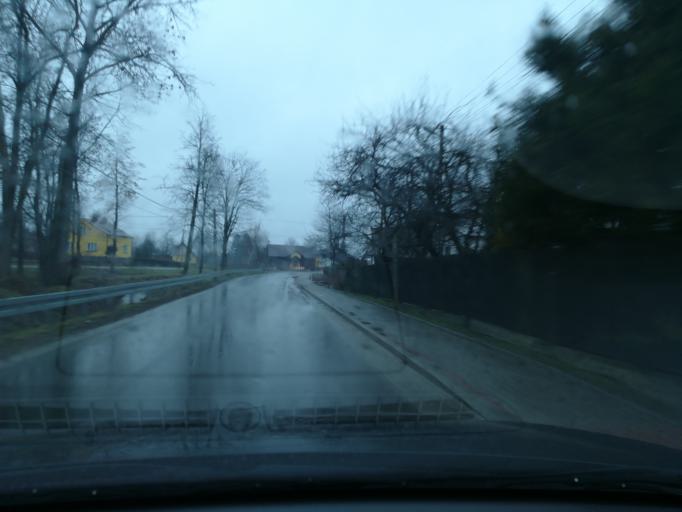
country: PL
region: Subcarpathian Voivodeship
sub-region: Powiat lancucki
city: Kosina
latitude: 50.0800
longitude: 22.3351
